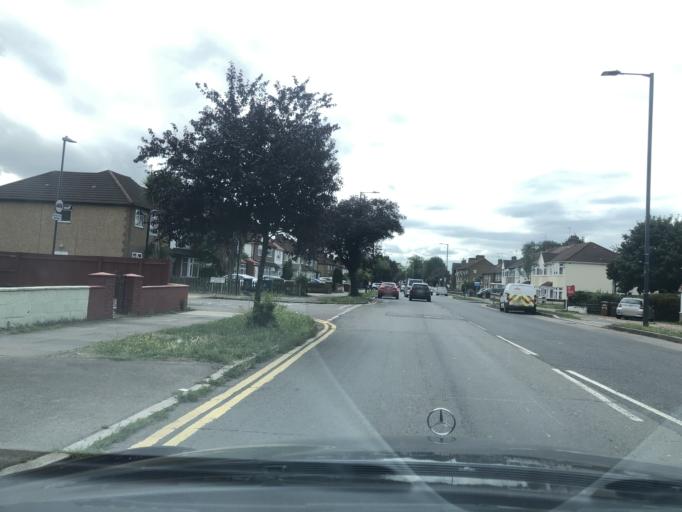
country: GB
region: England
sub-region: Greater London
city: Northolt
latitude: 51.5606
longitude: -0.3768
